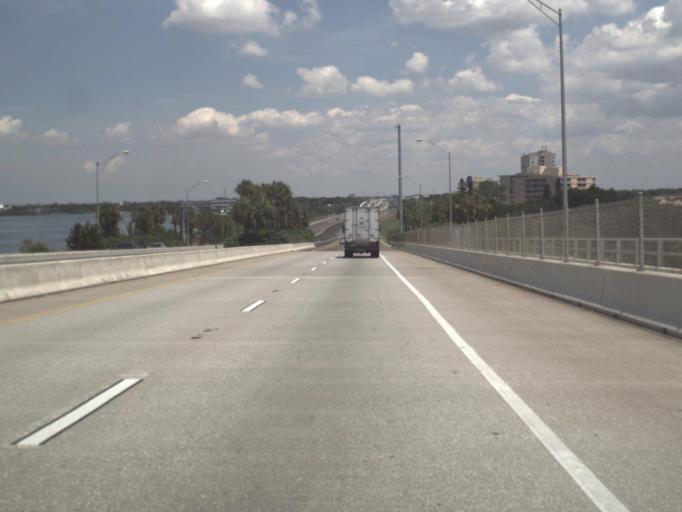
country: US
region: Florida
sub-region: Pinellas County
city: Tierra Verde
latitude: 27.6957
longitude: -82.6789
